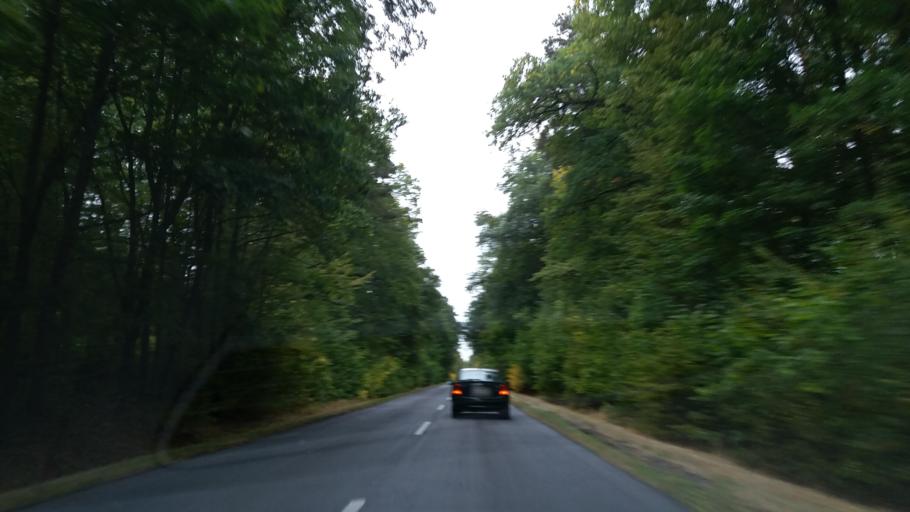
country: PL
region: Lubusz
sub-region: Powiat gorzowski
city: Klodawa
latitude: 52.8122
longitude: 15.2164
